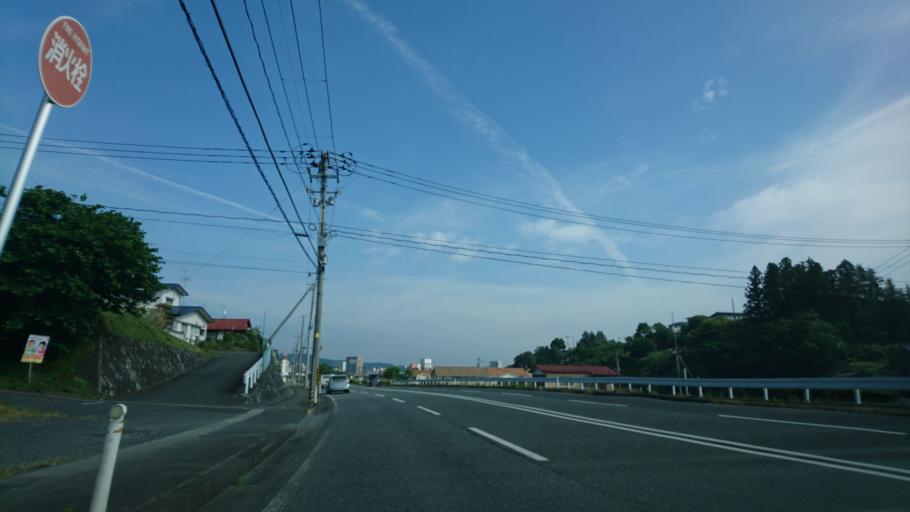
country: JP
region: Iwate
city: Ichinoseki
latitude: 38.9178
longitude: 141.1411
